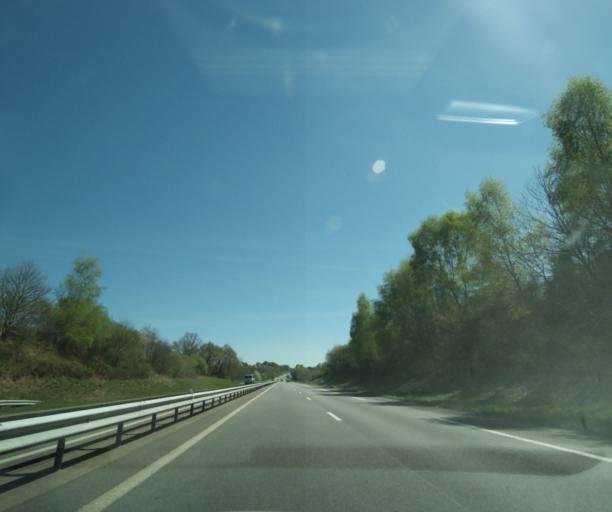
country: FR
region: Limousin
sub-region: Departement de la Haute-Vienne
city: Vicq-sur-Breuilh
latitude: 45.6335
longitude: 1.4294
